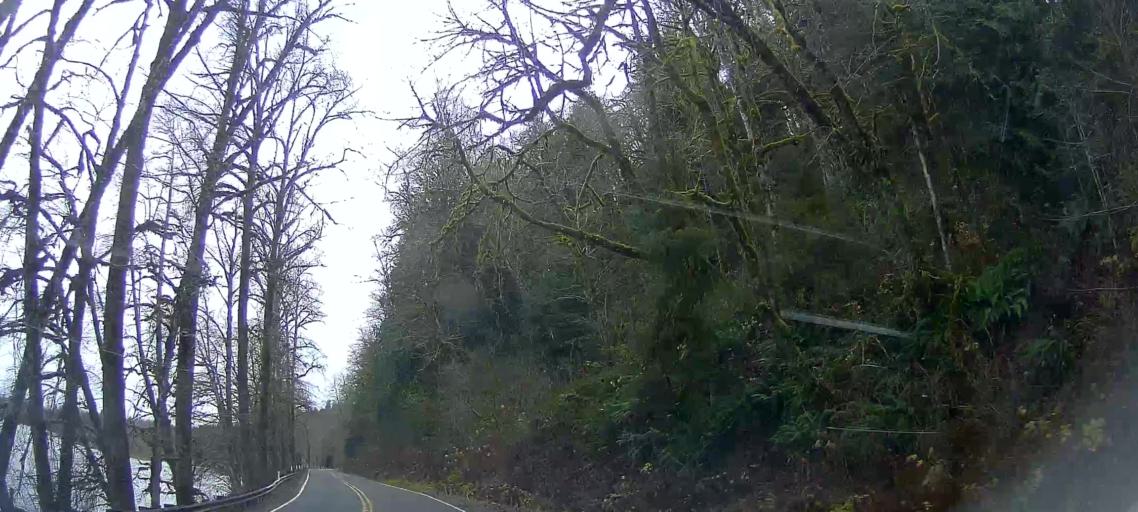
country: US
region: Washington
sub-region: Skagit County
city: Sedro-Woolley
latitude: 48.5102
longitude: -121.9020
